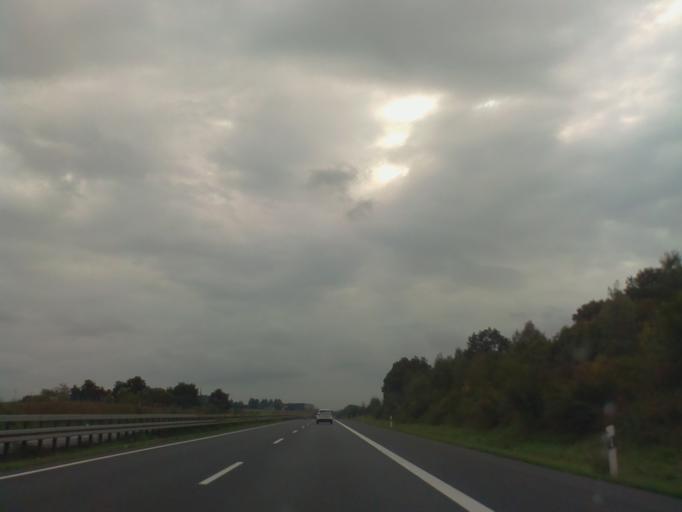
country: DE
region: Hesse
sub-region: Regierungsbezirk Kassel
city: Flieden
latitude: 50.4337
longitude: 9.5921
